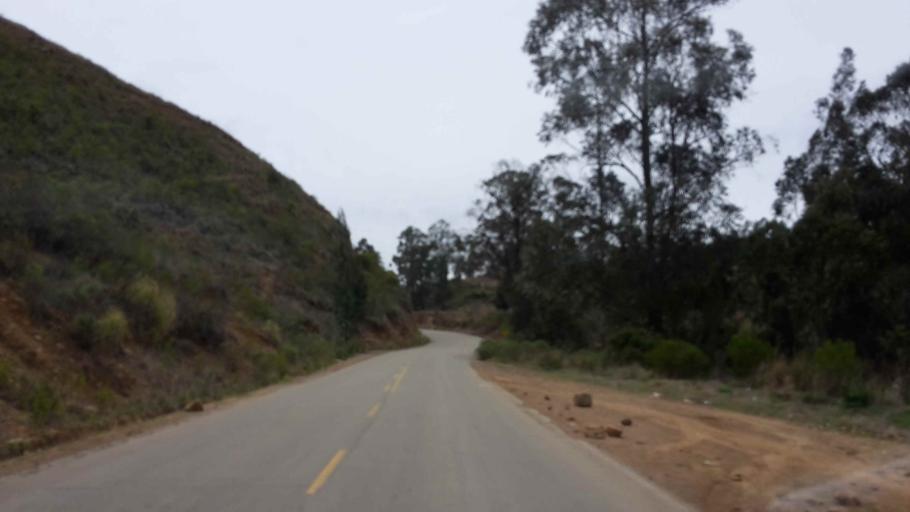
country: BO
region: Cochabamba
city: Totora
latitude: -17.7238
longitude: -65.1942
